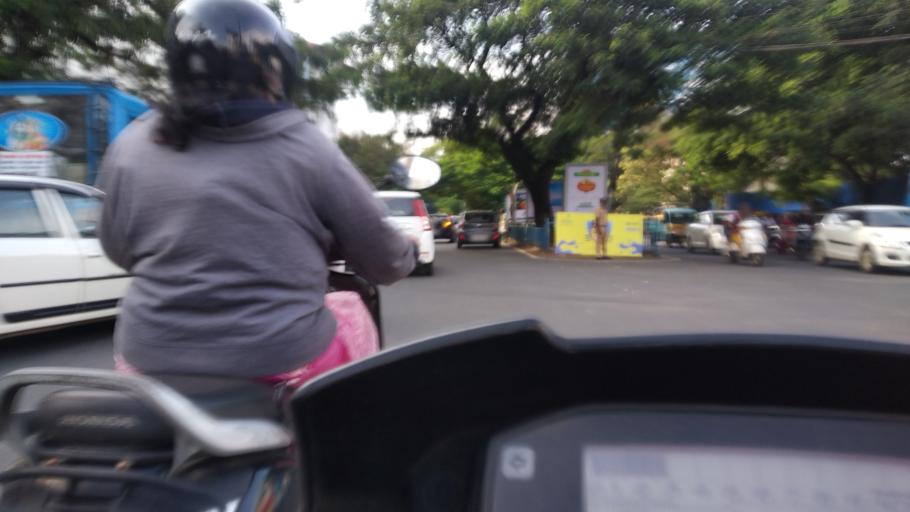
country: IN
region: Kerala
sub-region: Ernakulam
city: Cochin
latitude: 9.9838
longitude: 76.2739
